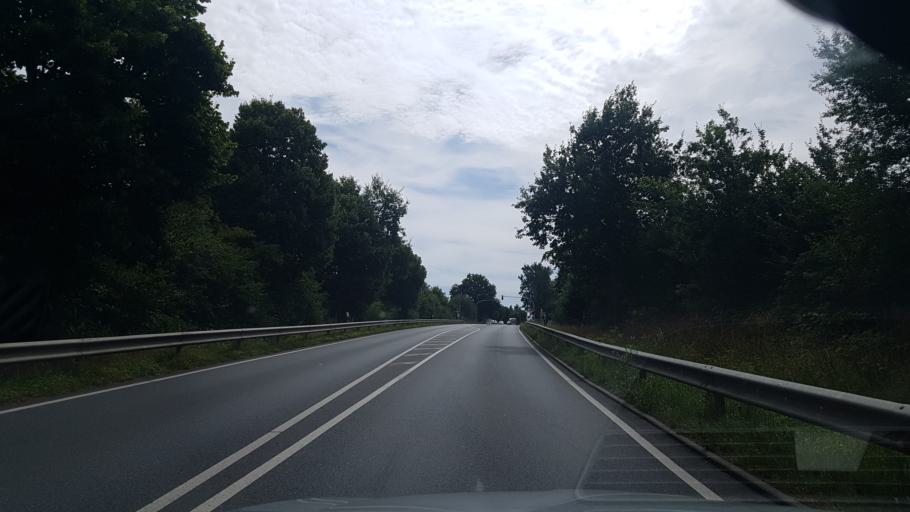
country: DE
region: Schleswig-Holstein
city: Reesdorf
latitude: 54.1857
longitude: 10.0493
